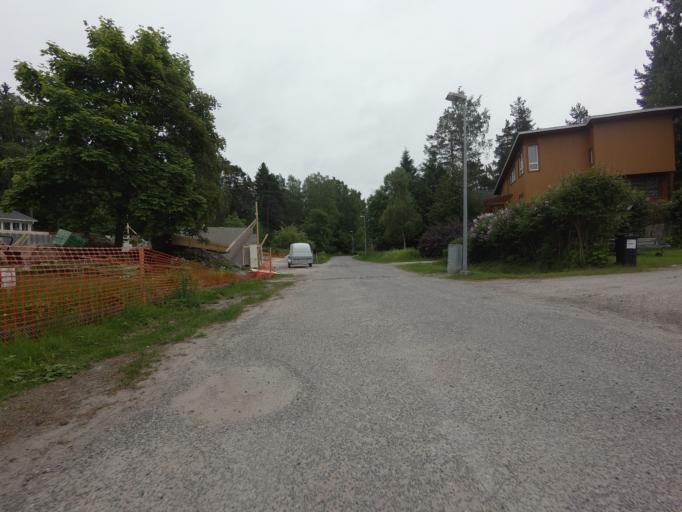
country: FI
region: Uusimaa
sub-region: Helsinki
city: Kauniainen
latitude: 60.1902
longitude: 24.7284
